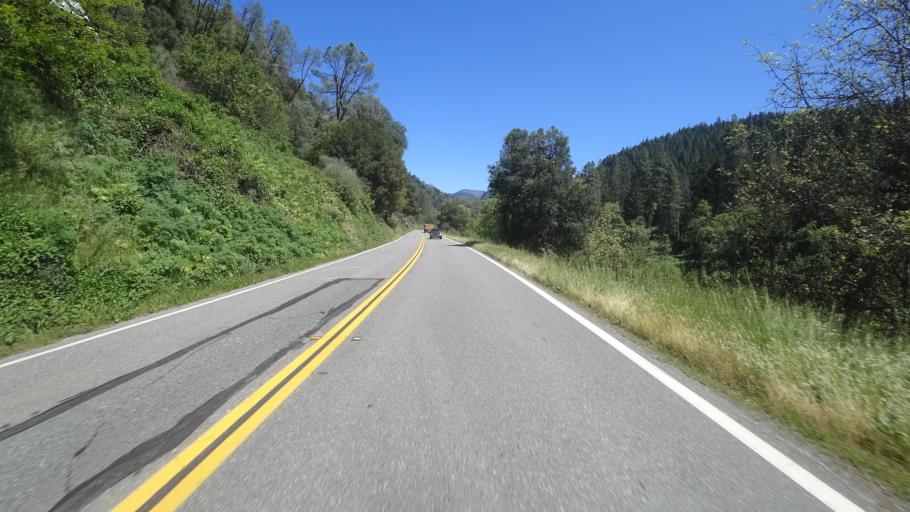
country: US
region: California
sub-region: Trinity County
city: Hayfork
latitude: 40.7393
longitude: -123.2497
